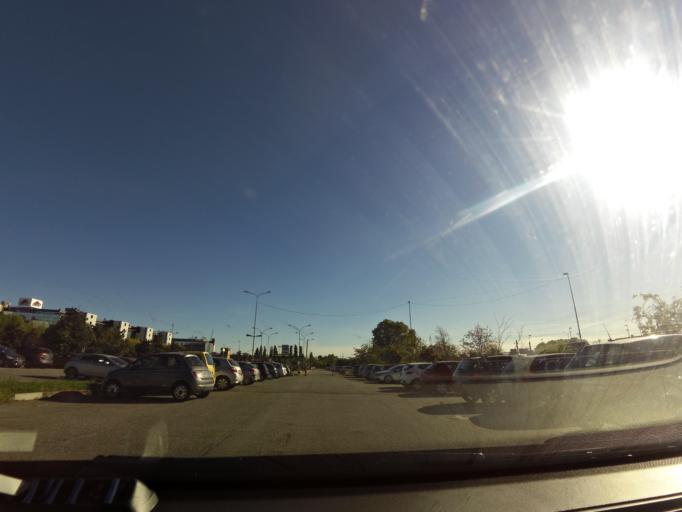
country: IT
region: Lombardy
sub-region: Citta metropolitana di Milano
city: Assago
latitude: 45.4016
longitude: 9.1461
